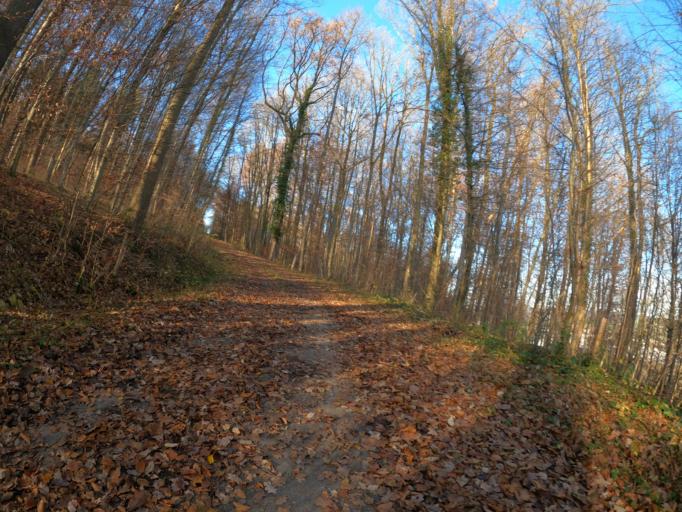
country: DE
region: Baden-Wuerttemberg
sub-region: Regierungsbezirk Stuttgart
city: Uhingen
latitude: 48.7051
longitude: 9.5729
